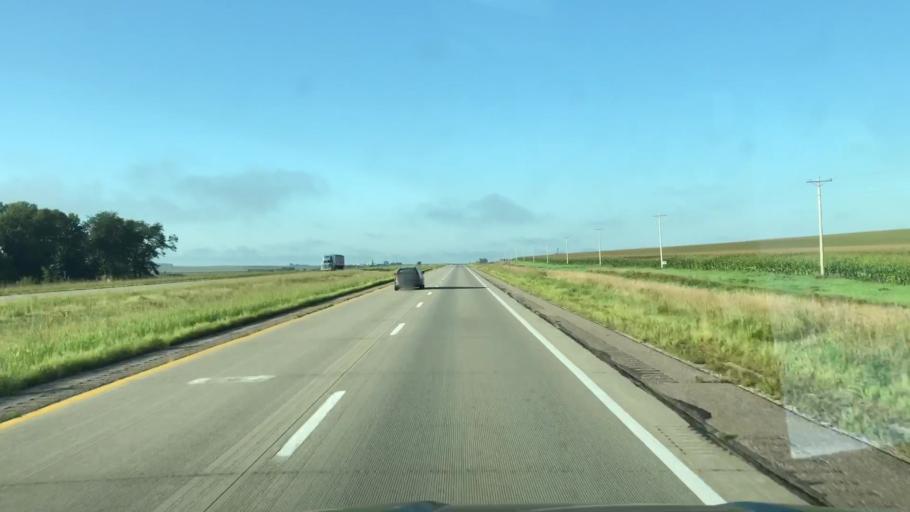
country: US
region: Iowa
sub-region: Sioux County
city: Alton
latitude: 42.9451
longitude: -96.0402
